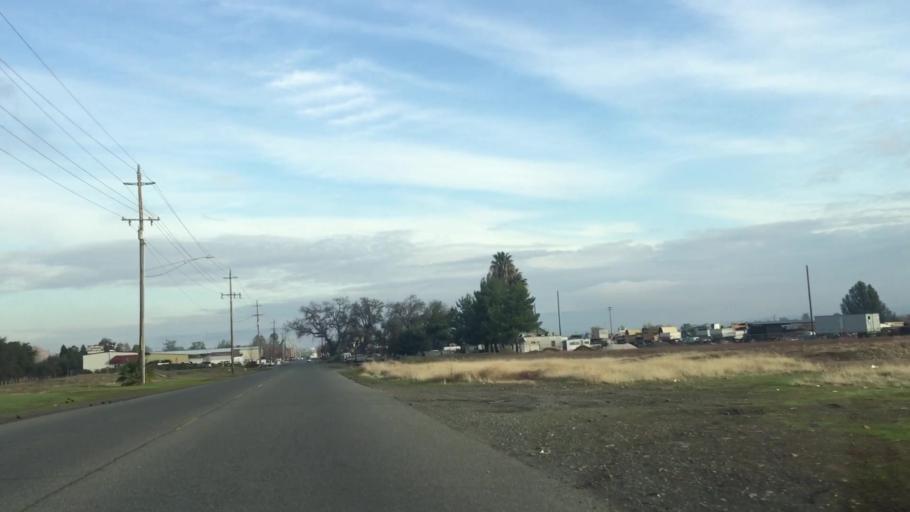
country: US
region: California
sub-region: Butte County
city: South Oroville
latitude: 39.4820
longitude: -121.5747
